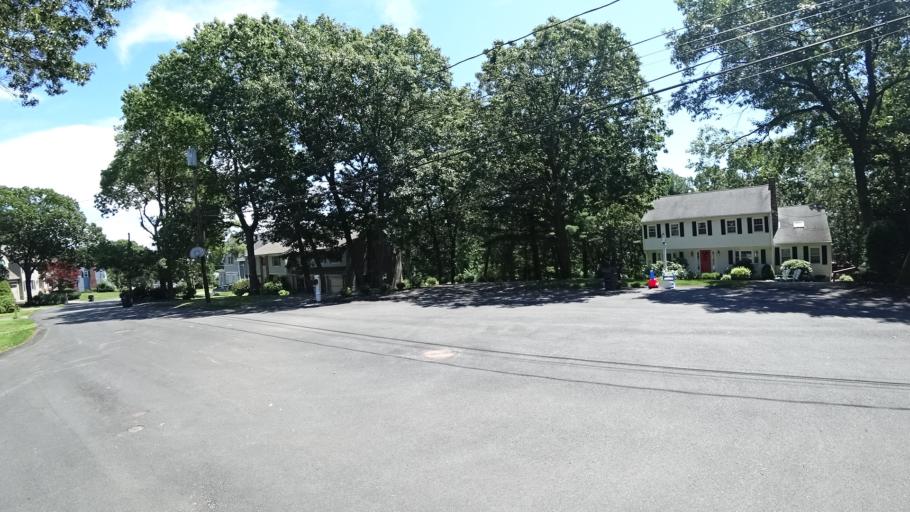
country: US
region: Massachusetts
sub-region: Norfolk County
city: Dedham
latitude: 42.2212
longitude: -71.1608
